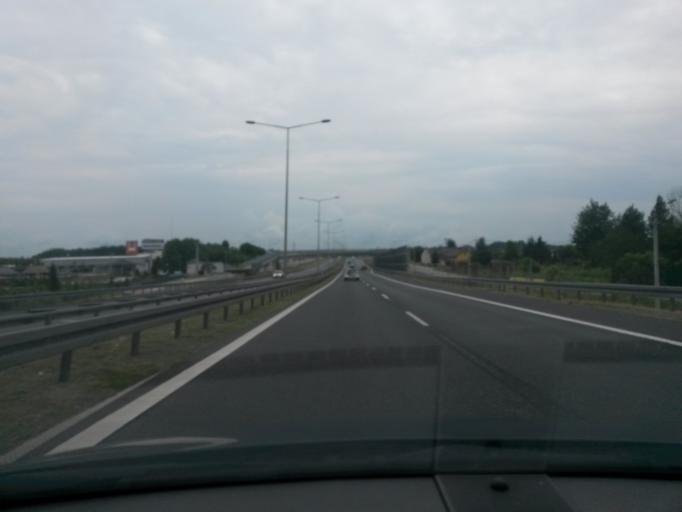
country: PL
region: Masovian Voivodeship
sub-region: Powiat zyrardowski
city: Mszczonow
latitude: 51.9424
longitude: 20.4827
